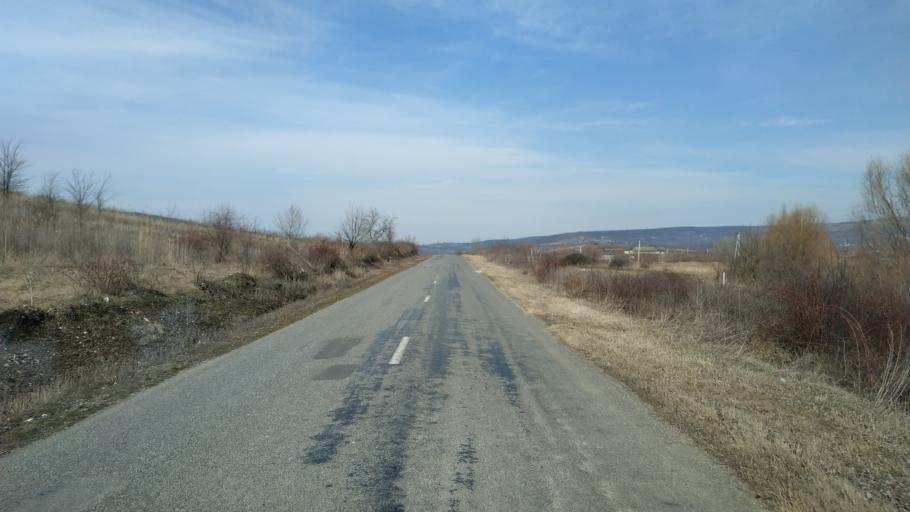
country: MD
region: Nisporeni
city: Nisporeni
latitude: 47.1643
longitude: 28.1008
